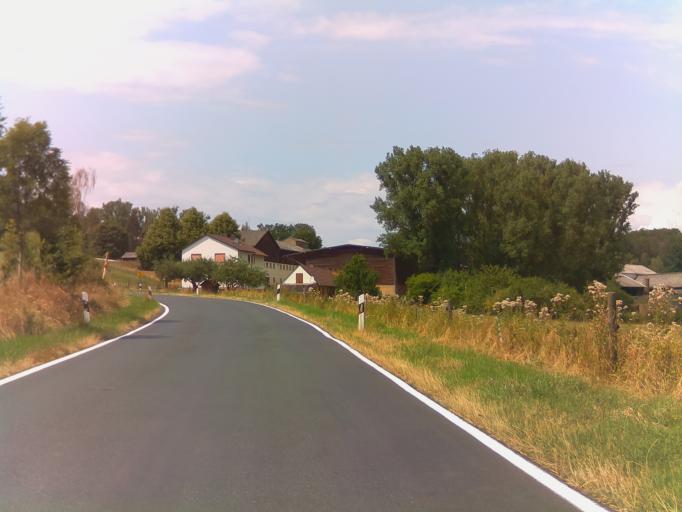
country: DE
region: Hesse
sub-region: Regierungsbezirk Giessen
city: Lauterbach
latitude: 50.5942
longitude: 9.4205
